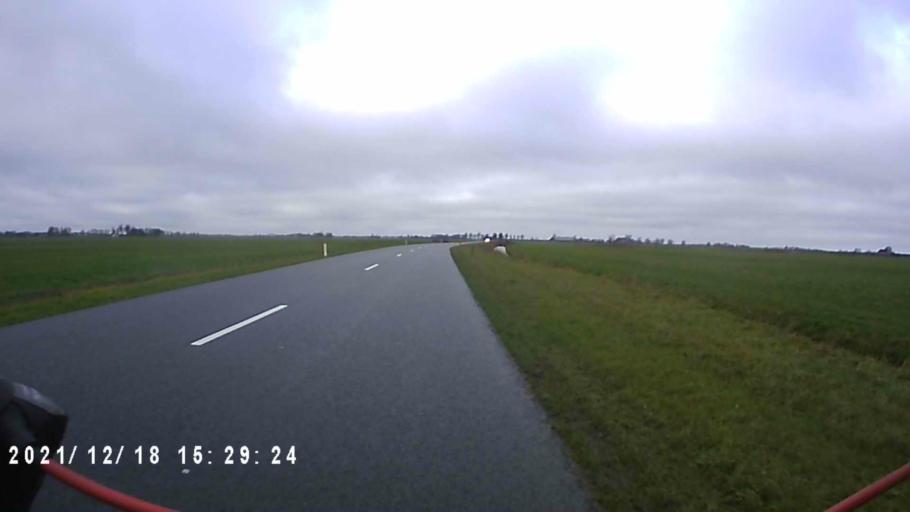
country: NL
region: Friesland
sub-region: Gemeente Dongeradeel
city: Anjum
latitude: 53.3342
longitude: 6.1415
